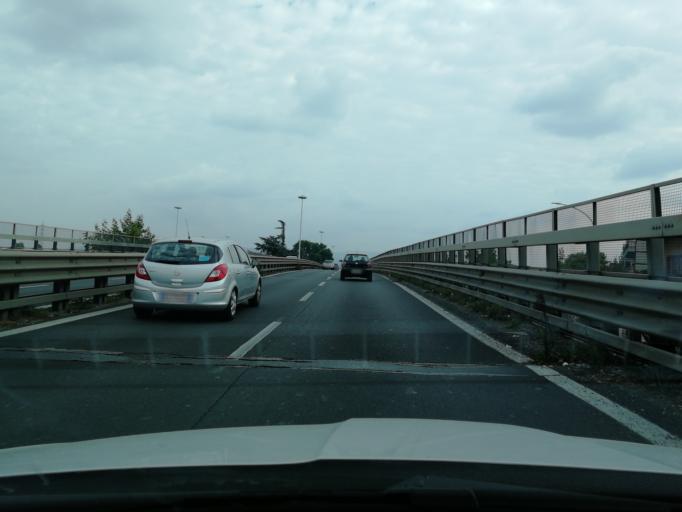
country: IT
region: Latium
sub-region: Citta metropolitana di Roma Capitale
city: Ciampino
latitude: 41.8437
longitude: 12.5826
